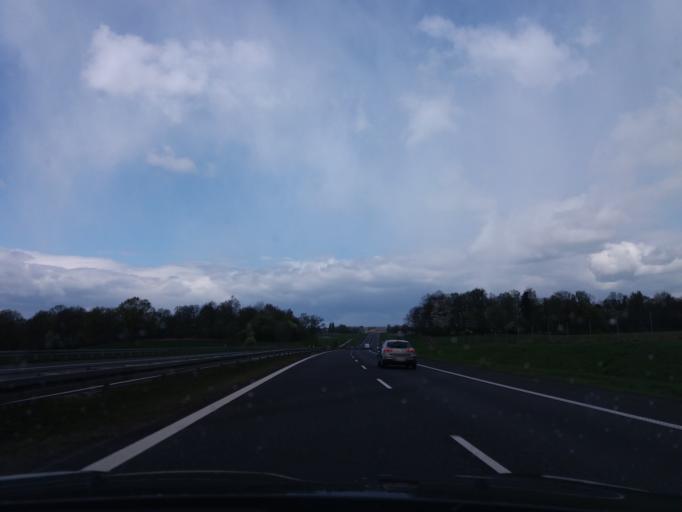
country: PL
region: Silesian Voivodeship
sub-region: Powiat gliwicki
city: Rudziniec
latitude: 50.4034
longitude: 18.4218
